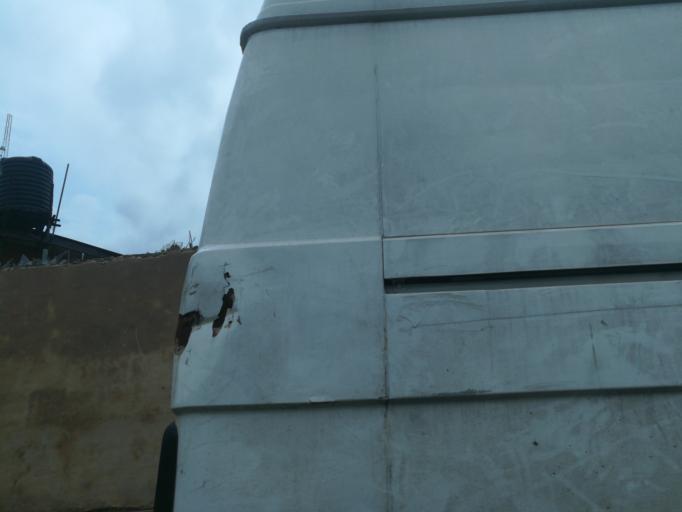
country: NG
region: Lagos
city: Ojota
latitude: 6.5691
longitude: 3.3632
